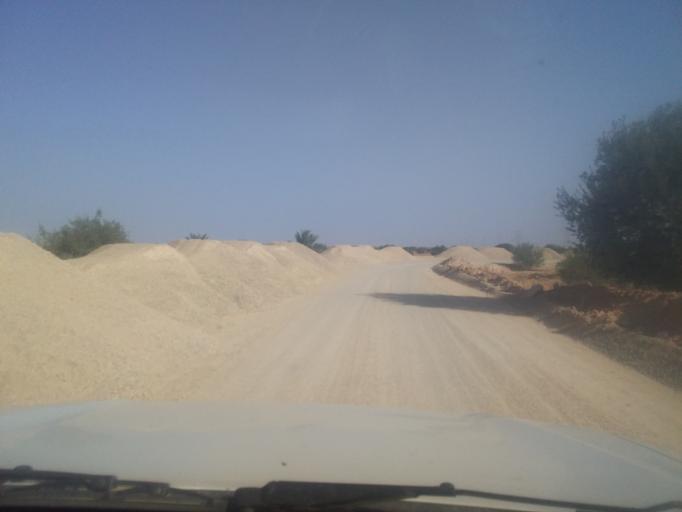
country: TN
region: Qabis
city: Matmata
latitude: 33.5876
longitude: 10.2696
